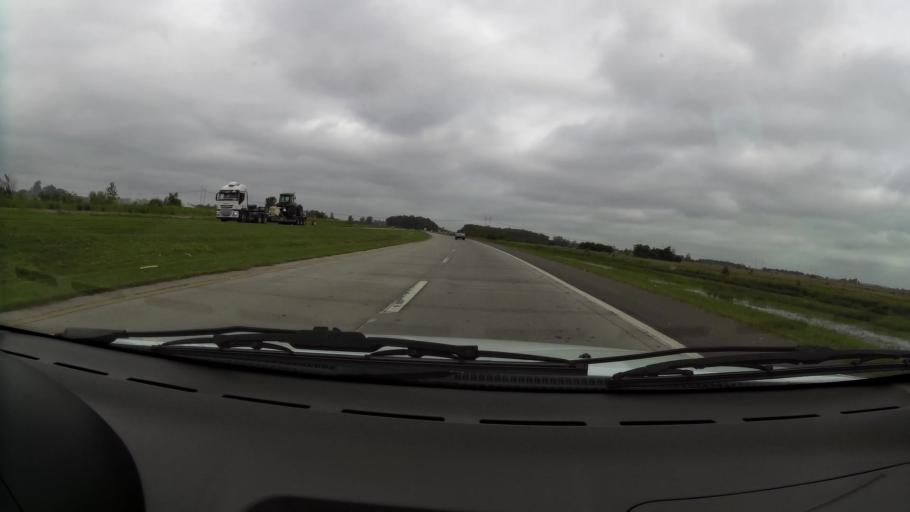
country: AR
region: Buenos Aires
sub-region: Partido de Brandsen
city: Brandsen
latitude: -35.0473
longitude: -58.1465
